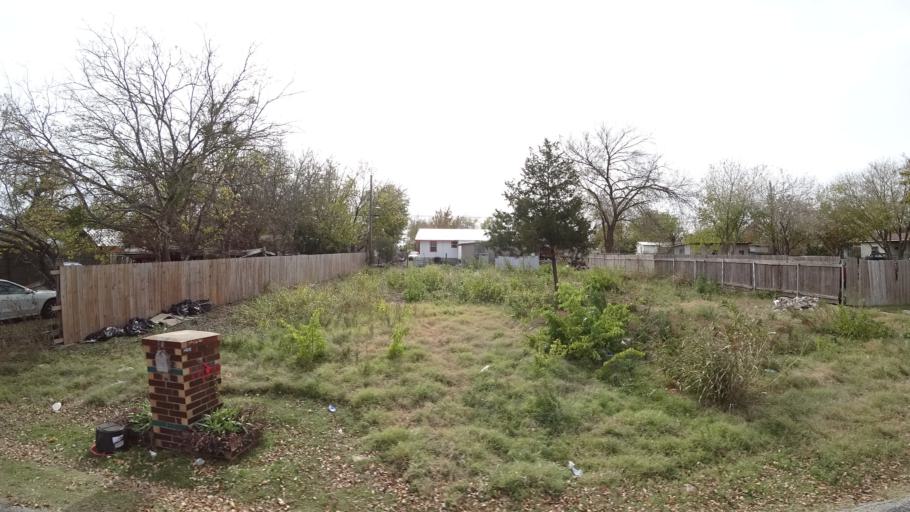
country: US
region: Texas
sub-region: Travis County
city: Garfield
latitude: 30.1307
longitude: -97.6168
